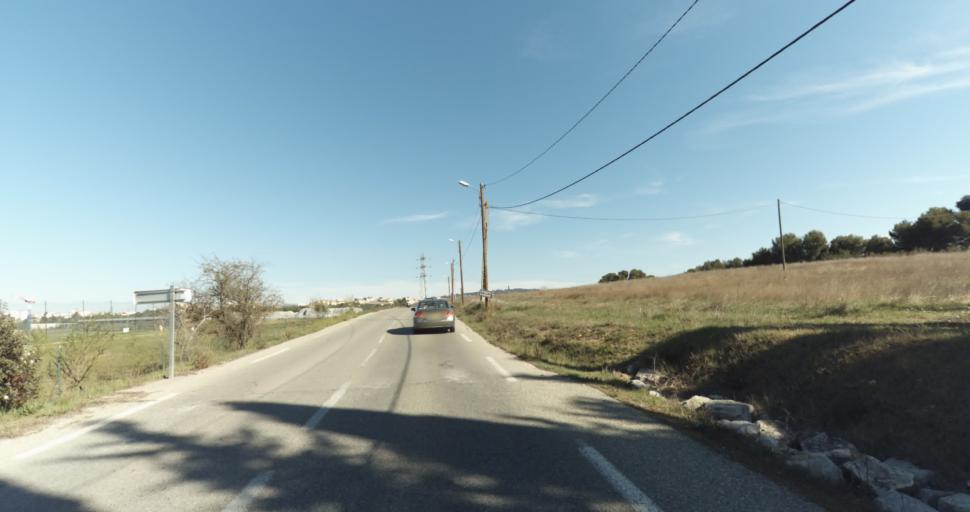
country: FR
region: Provence-Alpes-Cote d'Azur
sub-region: Departement des Bouches-du-Rhone
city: Aix-en-Provence
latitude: 43.5152
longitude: 5.4234
